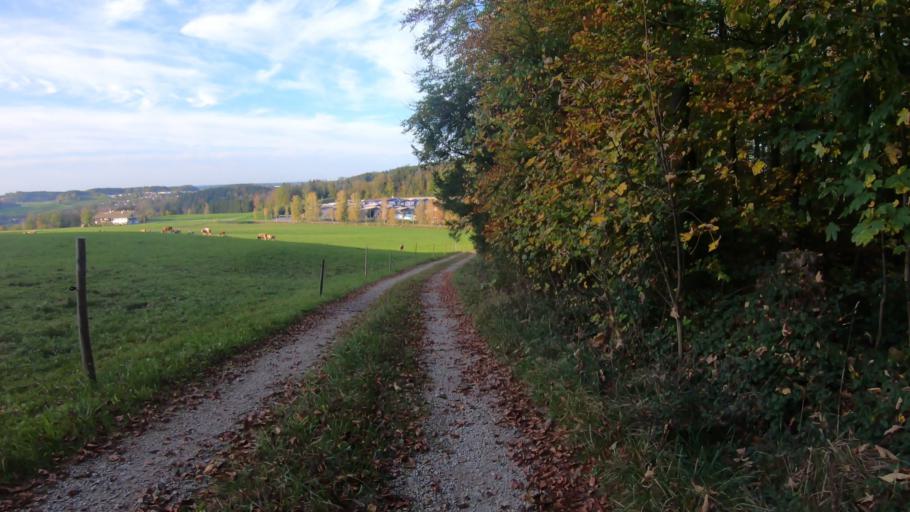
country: DE
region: Bavaria
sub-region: Upper Bavaria
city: Bergen
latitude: 47.8098
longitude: 12.6076
